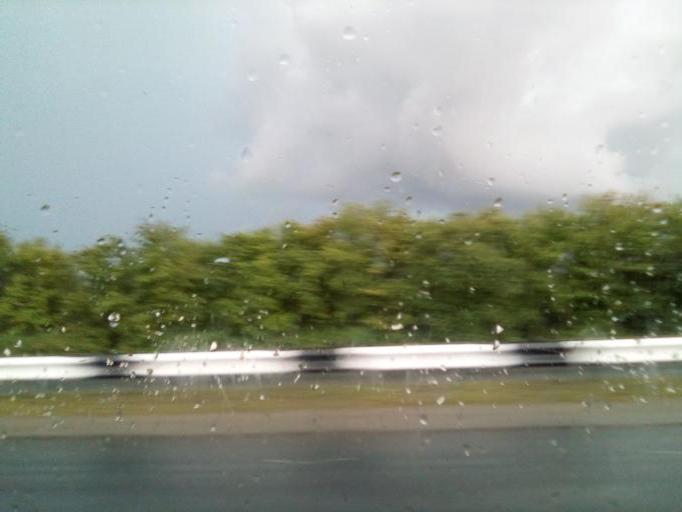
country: RU
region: Chelyabinsk
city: Poletayevo
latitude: 54.9670
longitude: 60.9509
